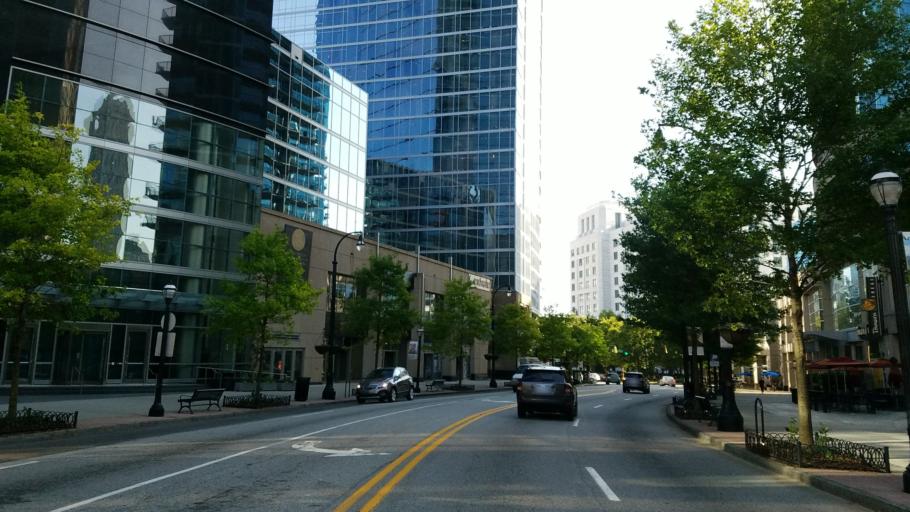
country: US
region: Georgia
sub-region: Fulton County
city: Atlanta
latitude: 33.7844
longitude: -84.3831
